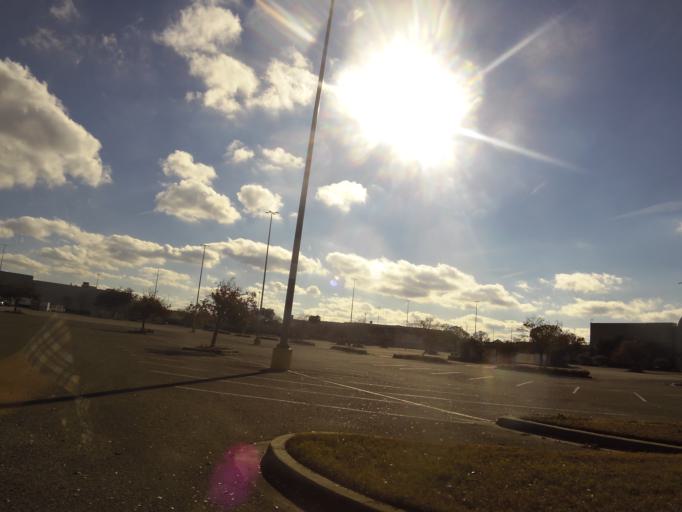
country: US
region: Florida
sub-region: Duval County
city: Jacksonville
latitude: 30.3258
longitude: -81.5527
